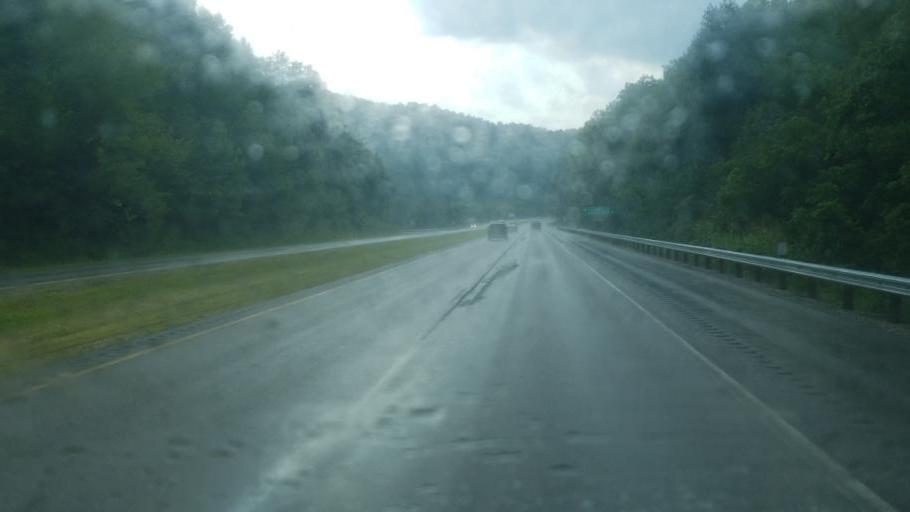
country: US
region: West Virginia
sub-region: Logan County
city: Chapmanville
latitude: 37.9856
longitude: -81.9516
